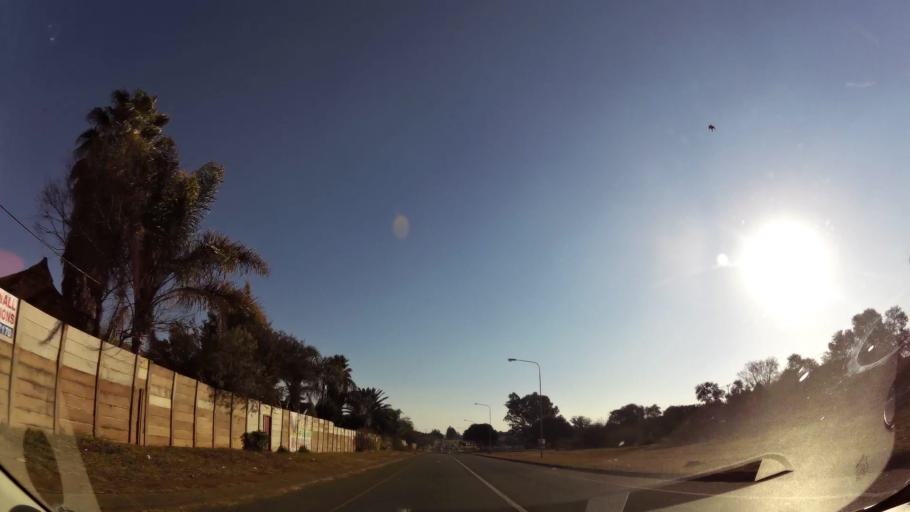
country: ZA
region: Gauteng
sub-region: City of Tshwane Metropolitan Municipality
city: Centurion
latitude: -25.8697
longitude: 28.1412
